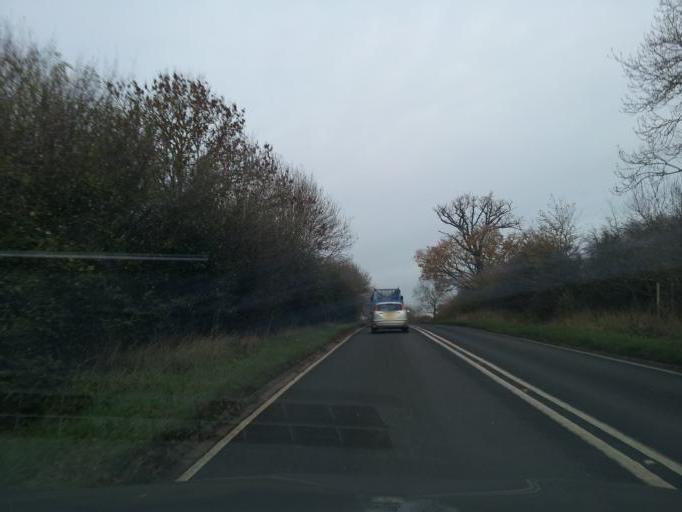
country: GB
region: England
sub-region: Buckinghamshire
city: Stewkley
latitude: 51.8657
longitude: -0.7603
